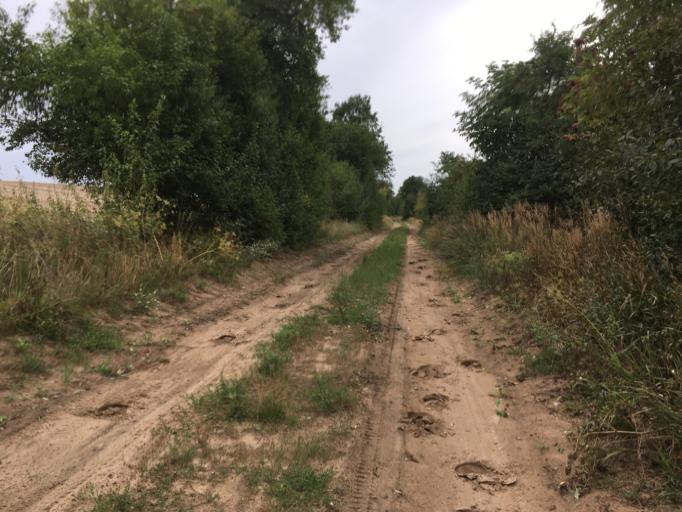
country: DE
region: Brandenburg
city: Passow
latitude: 53.1342
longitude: 14.1111
